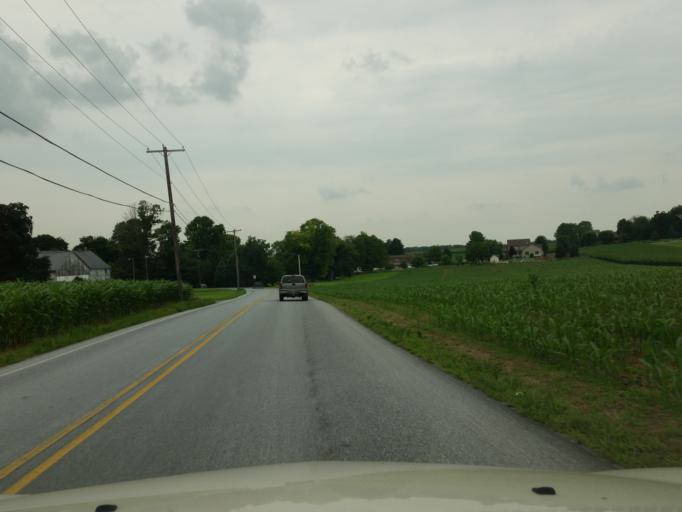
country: US
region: Pennsylvania
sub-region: Lancaster County
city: Lampeter
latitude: 40.0091
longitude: -76.2221
